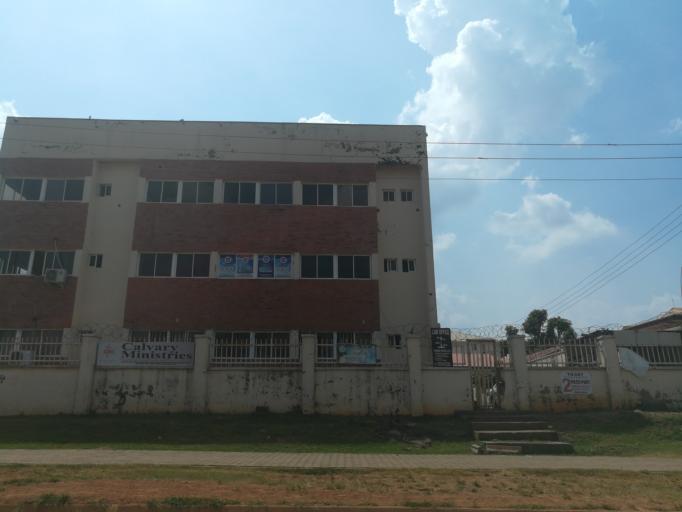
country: NG
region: Abuja Federal Capital Territory
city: Abuja
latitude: 9.0462
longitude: 7.4451
